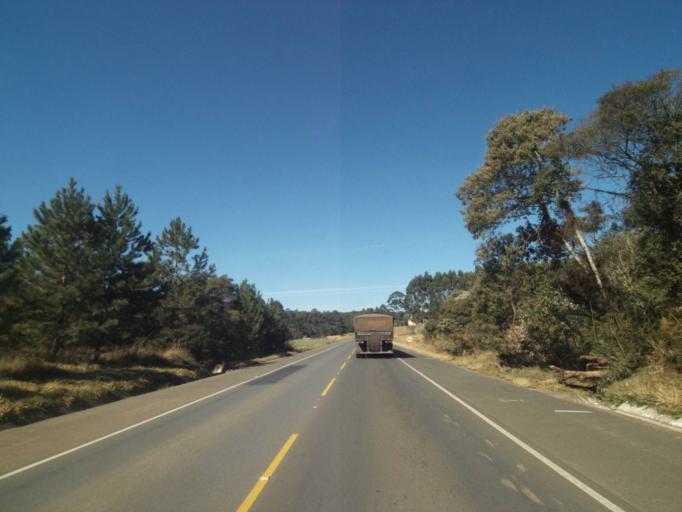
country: BR
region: Parana
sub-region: Tibagi
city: Tibagi
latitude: -24.5746
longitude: -50.4509
